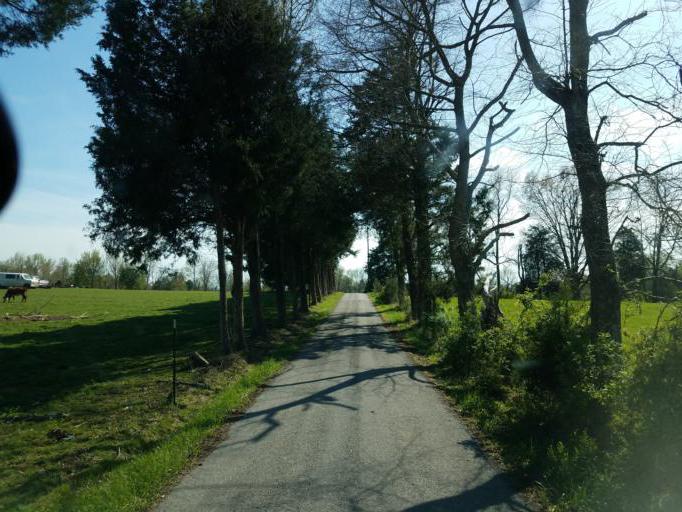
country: US
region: Kentucky
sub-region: Edmonson County
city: Brownsville
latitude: 37.1297
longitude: -86.1517
